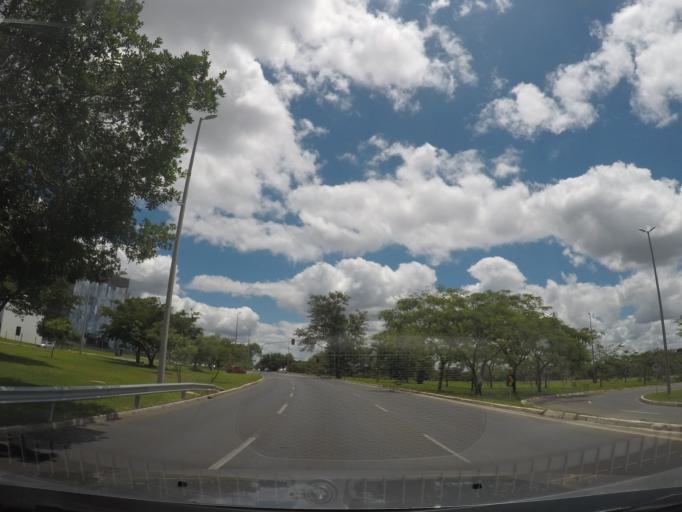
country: BR
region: Federal District
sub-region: Brasilia
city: Brasilia
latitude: -15.8096
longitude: -47.8606
